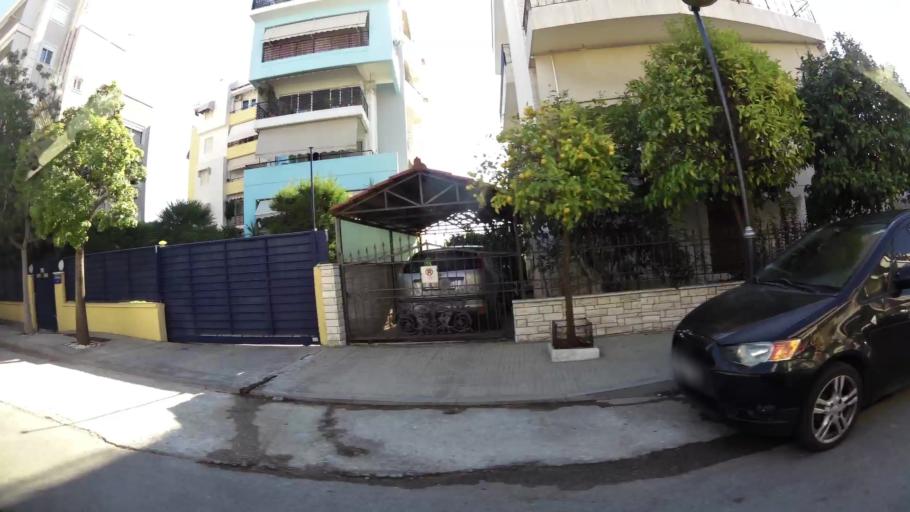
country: GR
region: Attica
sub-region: Nomarchia Athinas
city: Metamorfosi
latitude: 38.0638
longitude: 23.7690
